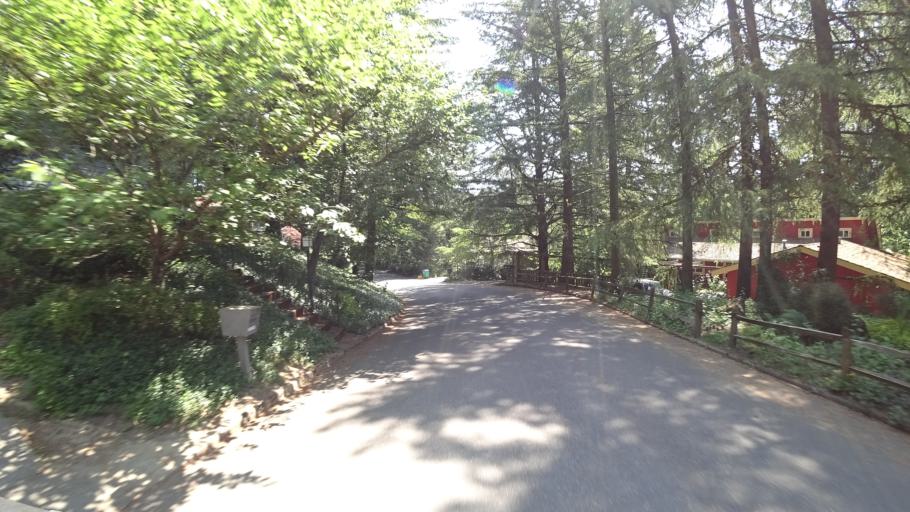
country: US
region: Oregon
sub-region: Washington County
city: West Slope
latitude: 45.5142
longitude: -122.7265
